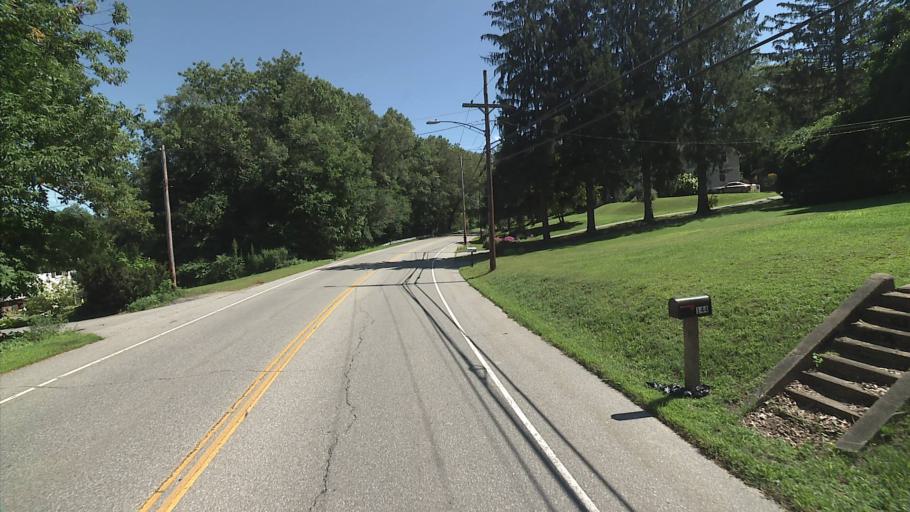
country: US
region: Connecticut
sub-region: New London County
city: Baltic
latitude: 41.6039
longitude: -72.0573
